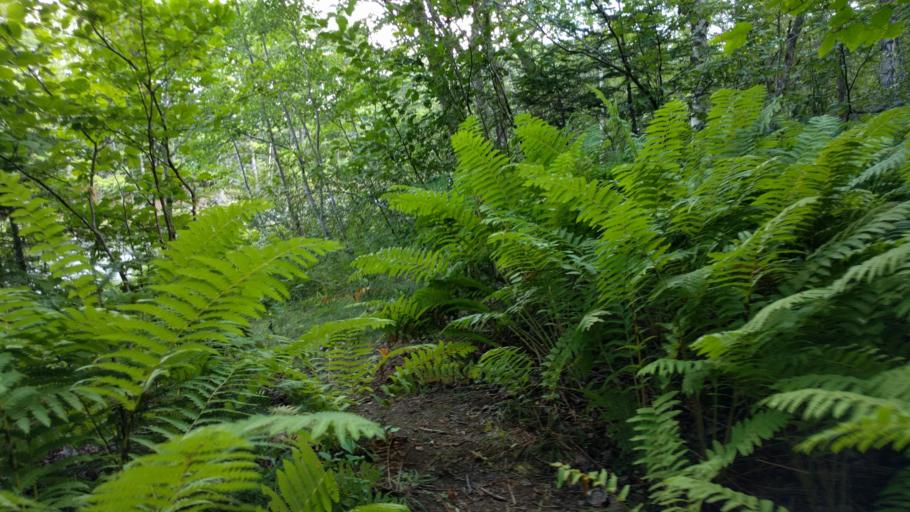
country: US
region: Maine
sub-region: Penobscot County
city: Patten
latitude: 46.0863
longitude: -68.7751
